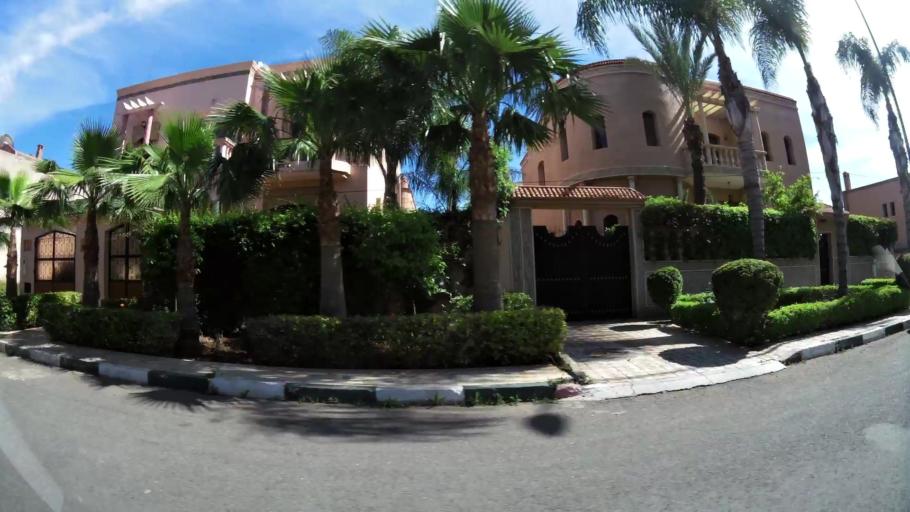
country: MA
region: Marrakech-Tensift-Al Haouz
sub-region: Marrakech
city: Marrakesh
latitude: 31.6521
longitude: -8.0551
